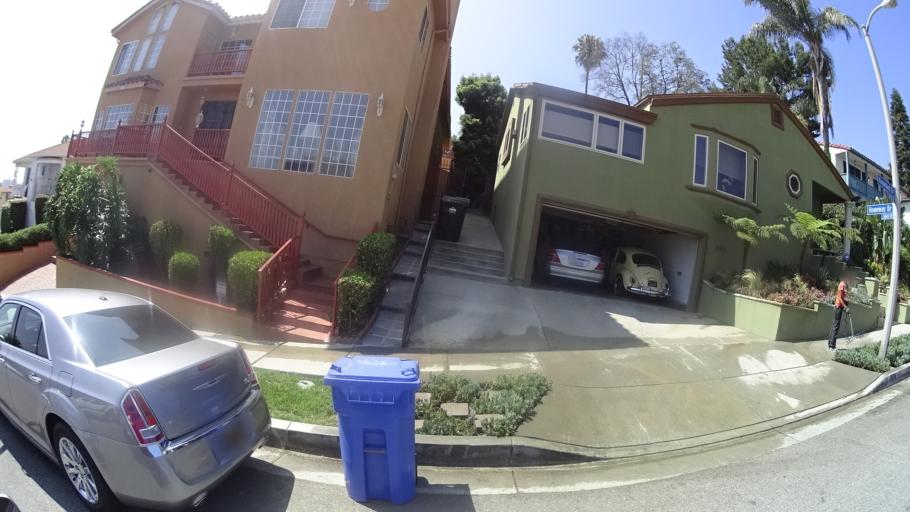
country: US
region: California
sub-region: Los Angeles County
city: View Park-Windsor Hills
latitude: 34.0037
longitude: -118.3372
